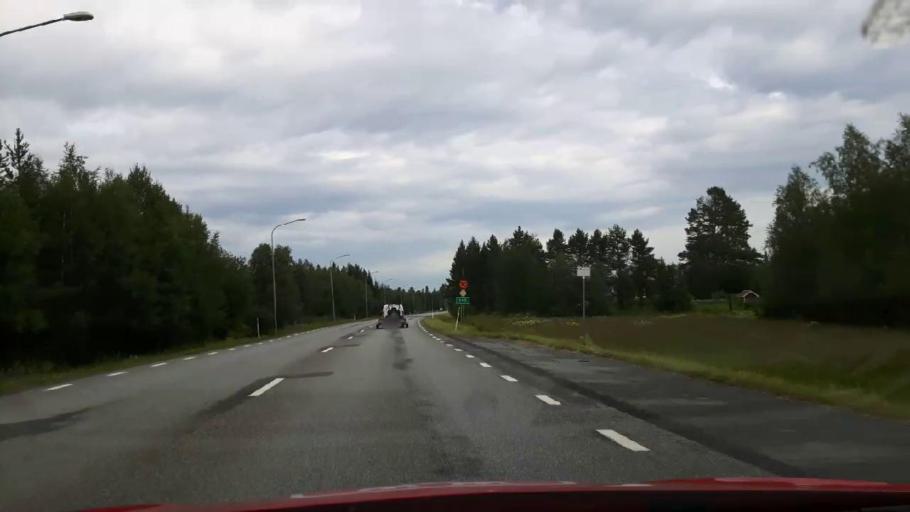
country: SE
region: Jaemtland
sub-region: Stroemsunds Kommun
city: Stroemsund
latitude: 63.6723
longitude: 15.3927
